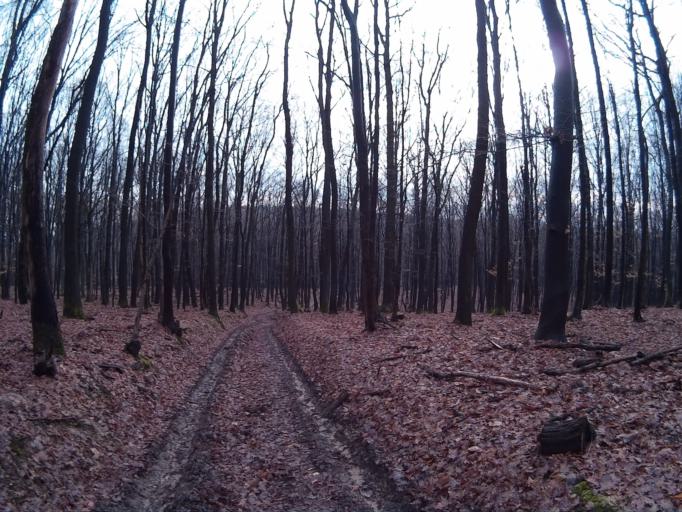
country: HU
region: Borsod-Abauj-Zemplen
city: Satoraljaujhely
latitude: 48.4184
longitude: 21.5791
